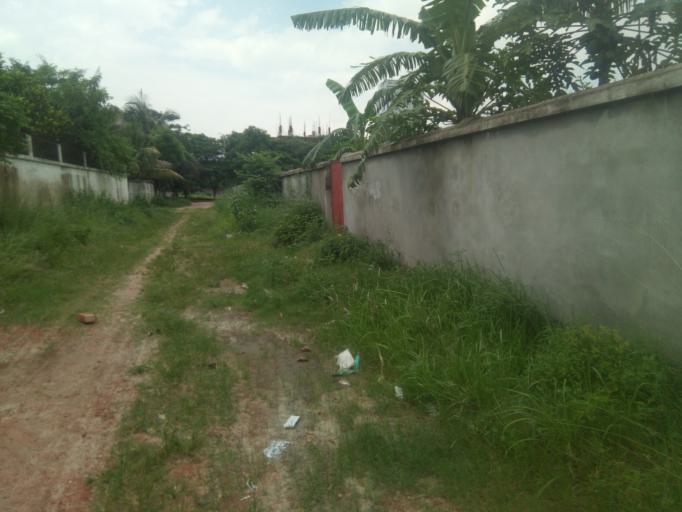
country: BD
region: Dhaka
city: Azimpur
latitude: 23.7512
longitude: 90.3463
